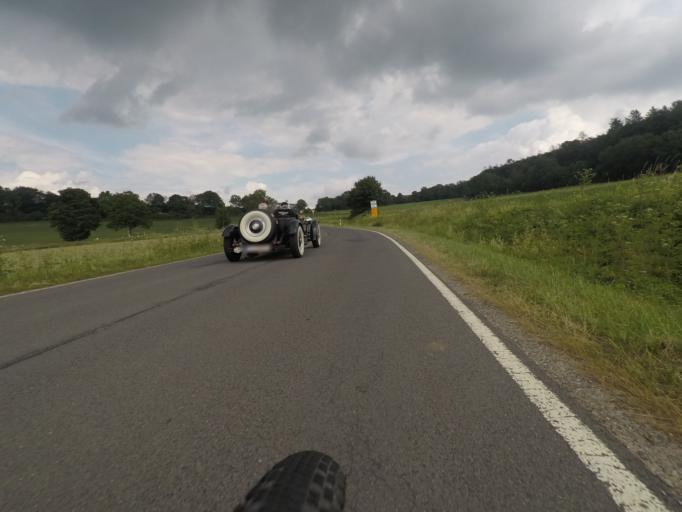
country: DE
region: Hesse
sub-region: Regierungsbezirk Kassel
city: Grossalmerode
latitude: 51.2135
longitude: 9.8203
